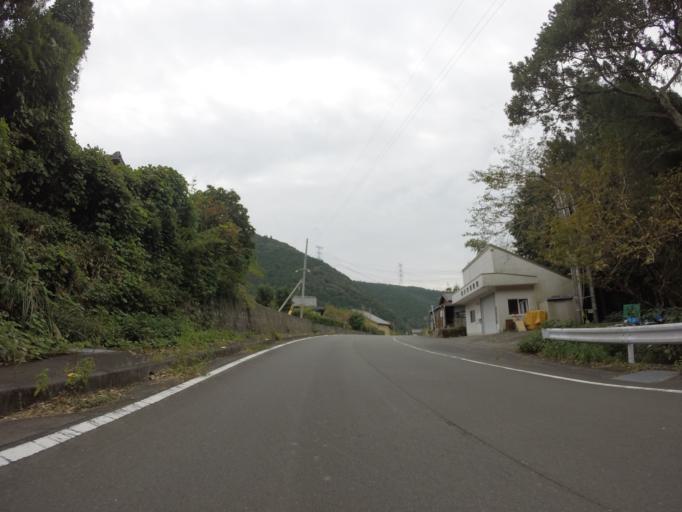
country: JP
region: Shizuoka
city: Mori
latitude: 34.8659
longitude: 138.0179
